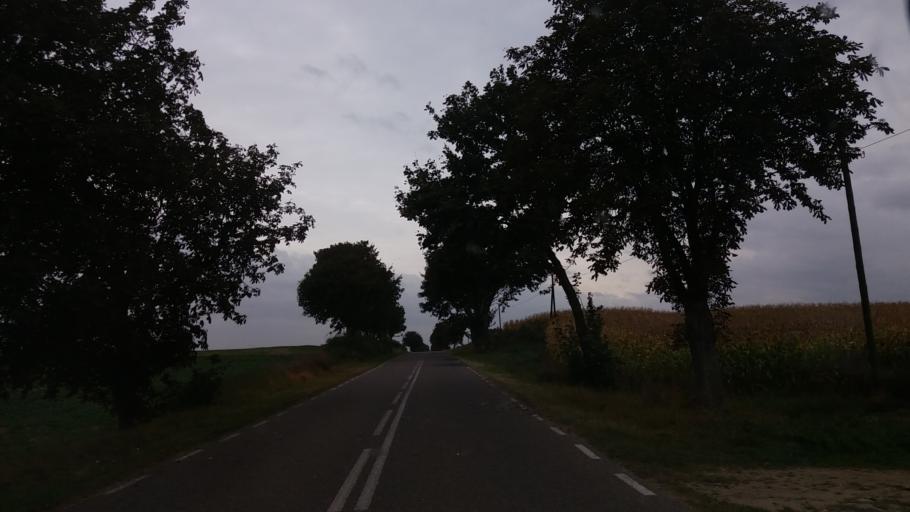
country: PL
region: Lubusz
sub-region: Powiat strzelecko-drezdenecki
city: Strzelce Krajenskie
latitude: 52.9616
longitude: 15.5787
